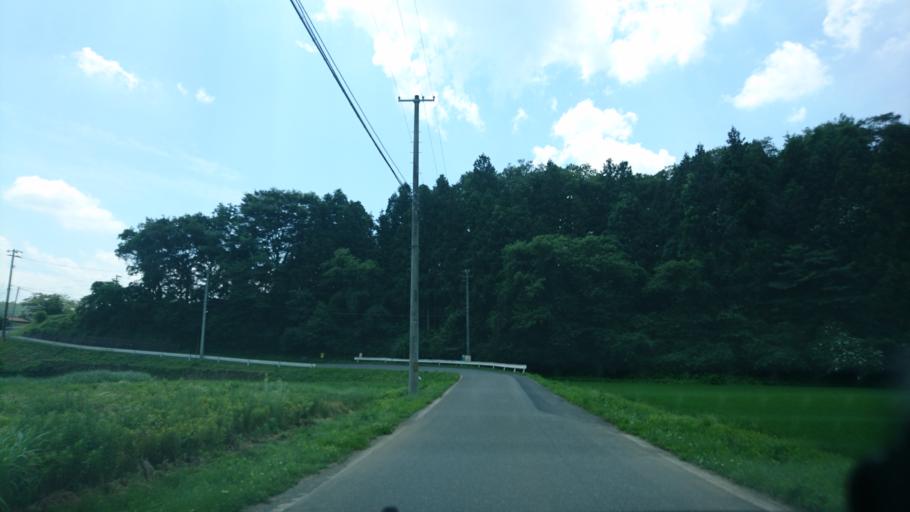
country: JP
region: Iwate
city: Ichinoseki
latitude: 38.9100
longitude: 141.2239
